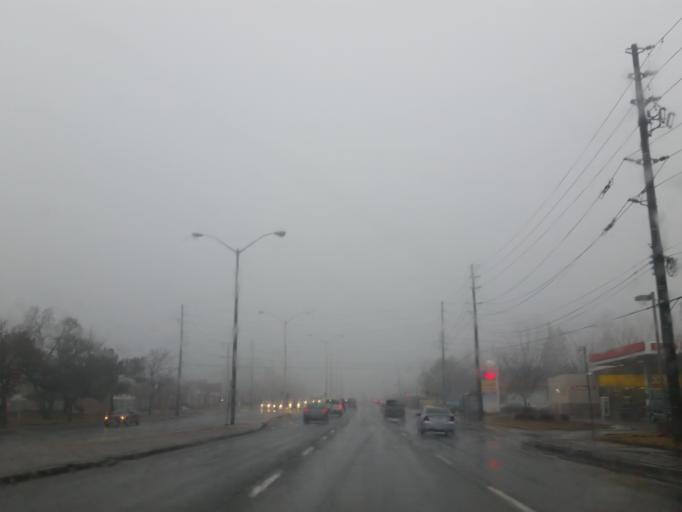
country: CA
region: Ontario
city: Scarborough
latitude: 43.7488
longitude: -79.2070
